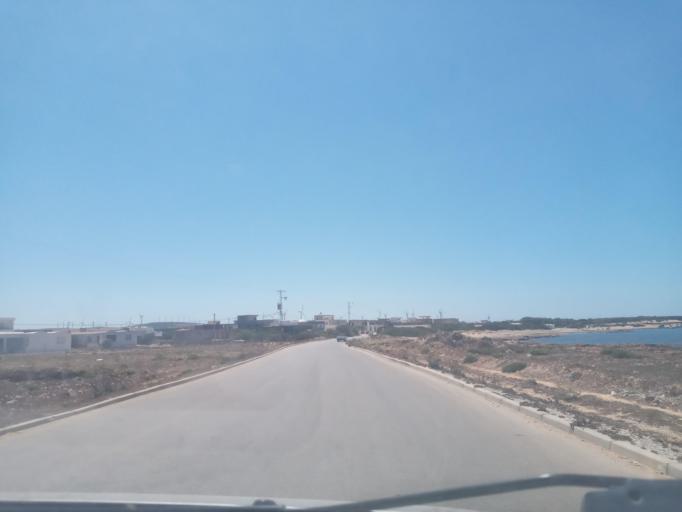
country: TN
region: Nabul
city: El Haouaria
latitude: 37.0495
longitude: 10.9740
